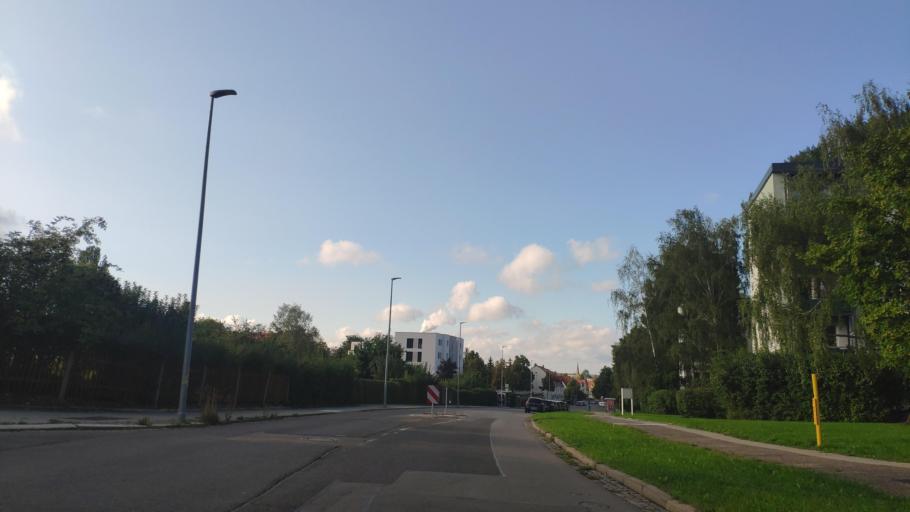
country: DE
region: Saxony
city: Chemnitz
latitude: 50.8199
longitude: 12.9577
